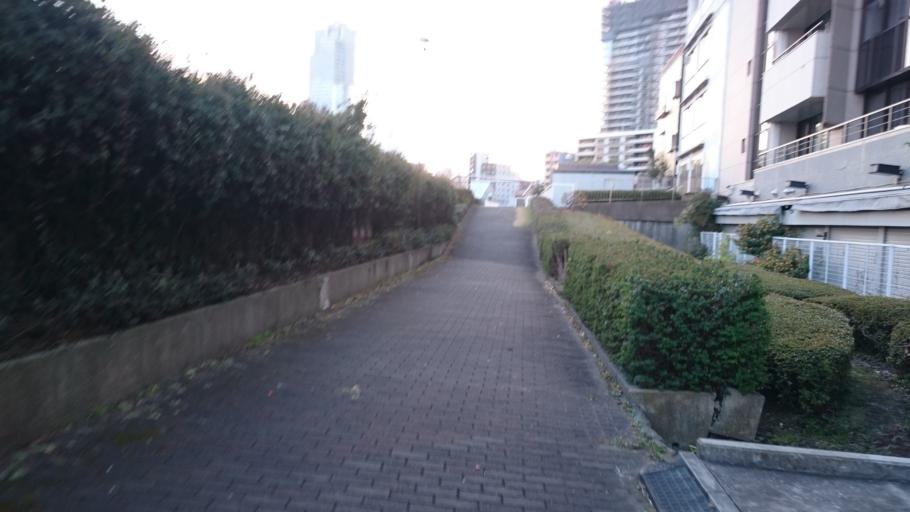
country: JP
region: Tokyo
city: Tokyo
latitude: 35.6724
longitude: 139.7837
